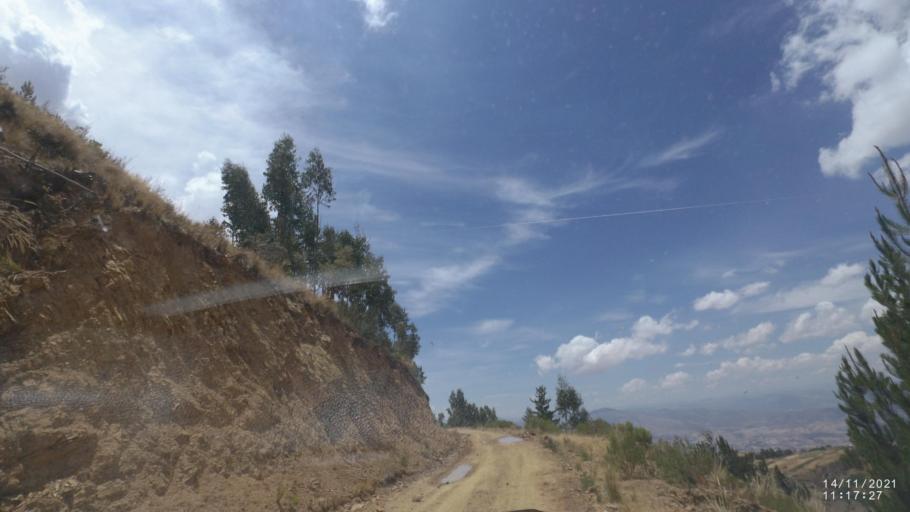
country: BO
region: Cochabamba
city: Cochabamba
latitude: -17.3310
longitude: -66.0451
